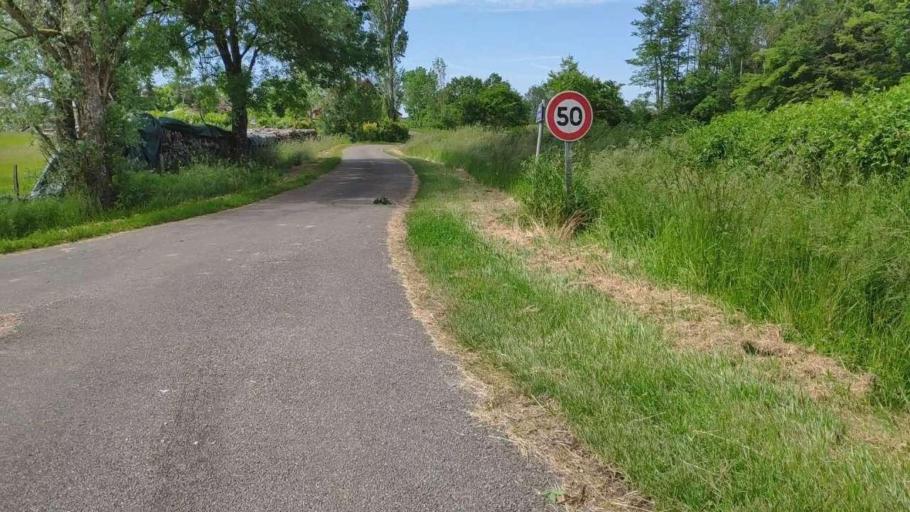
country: FR
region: Franche-Comte
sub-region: Departement du Jura
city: Bletterans
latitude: 46.6864
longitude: 5.4140
